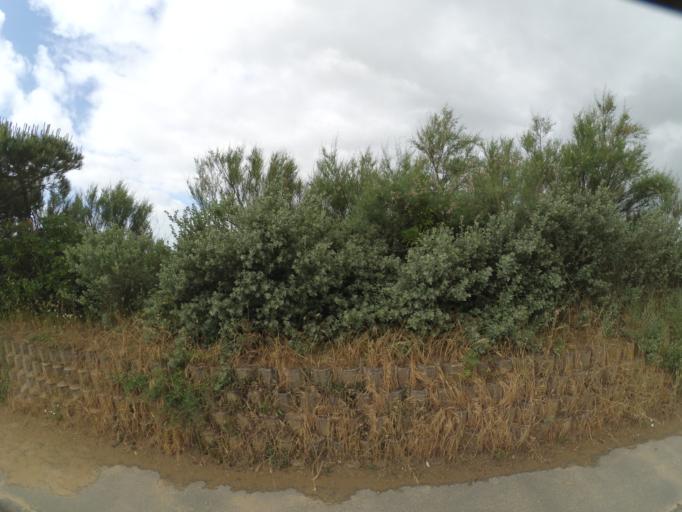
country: FR
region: Poitou-Charentes
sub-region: Departement de la Charente-Maritime
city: Aytre
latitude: 46.1253
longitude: -1.1266
